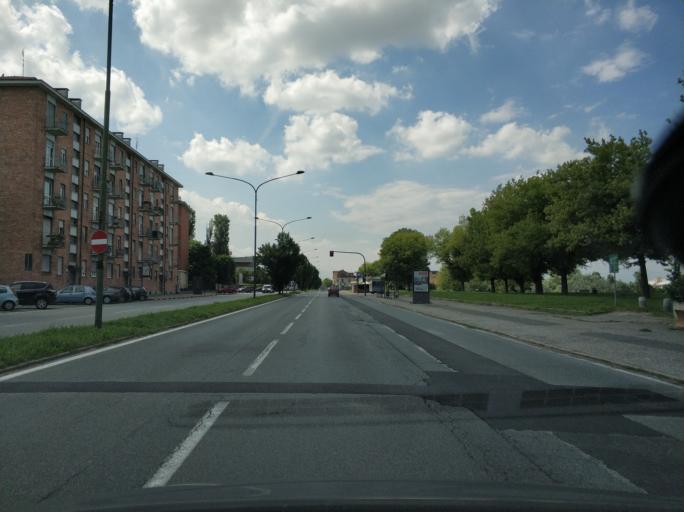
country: IT
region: Piedmont
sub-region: Provincia di Torino
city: Turin
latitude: 45.0963
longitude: 7.7143
